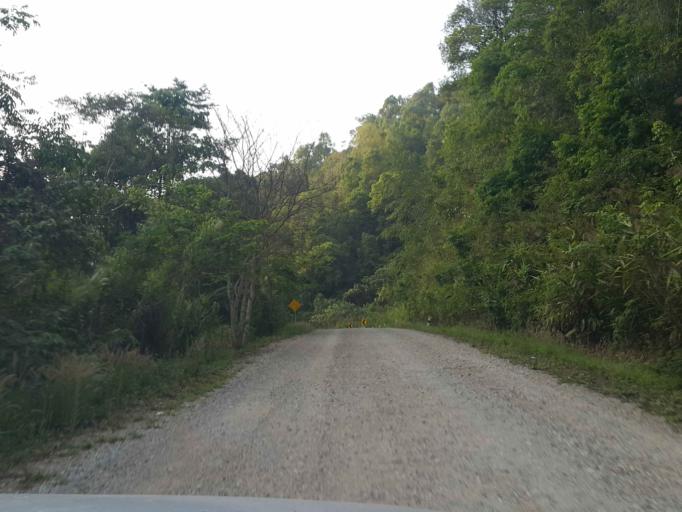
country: TH
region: Chiang Mai
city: Mae On
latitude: 18.9526
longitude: 99.3453
